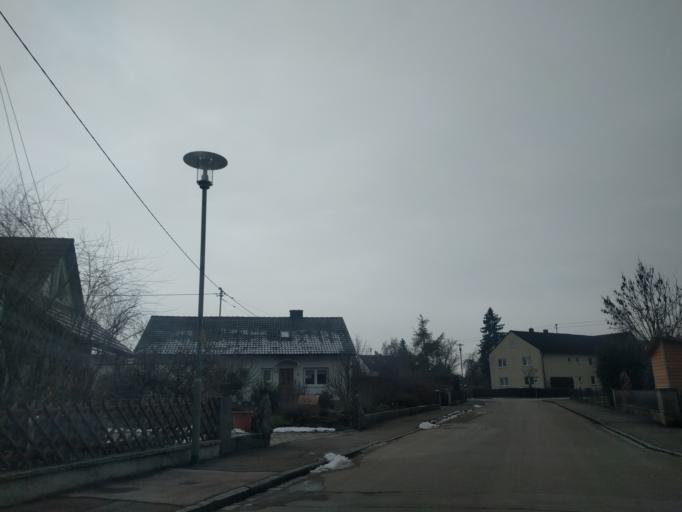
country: DE
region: Bavaria
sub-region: Swabia
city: Rain
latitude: 48.6912
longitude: 10.9074
